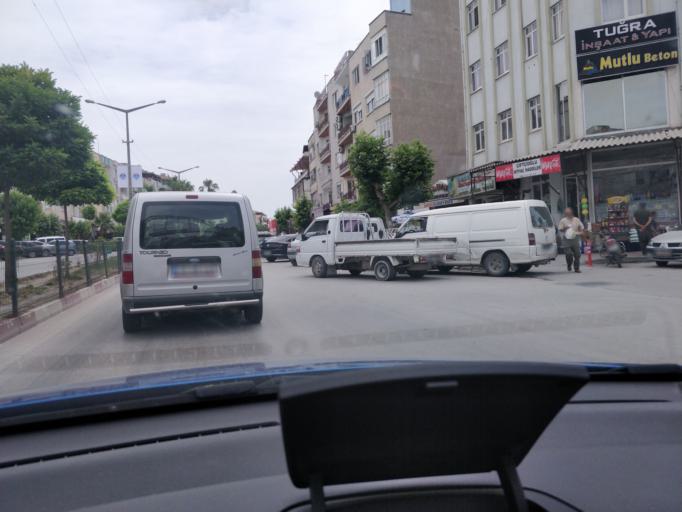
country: TR
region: Mersin
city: Mut
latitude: 36.6450
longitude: 33.4376
